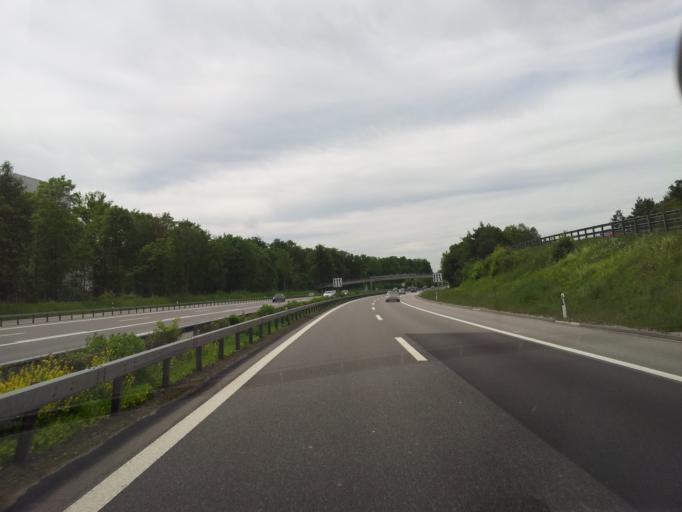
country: CH
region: Bern
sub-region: Bern-Mittelland District
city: Koniz
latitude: 46.9530
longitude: 7.4138
